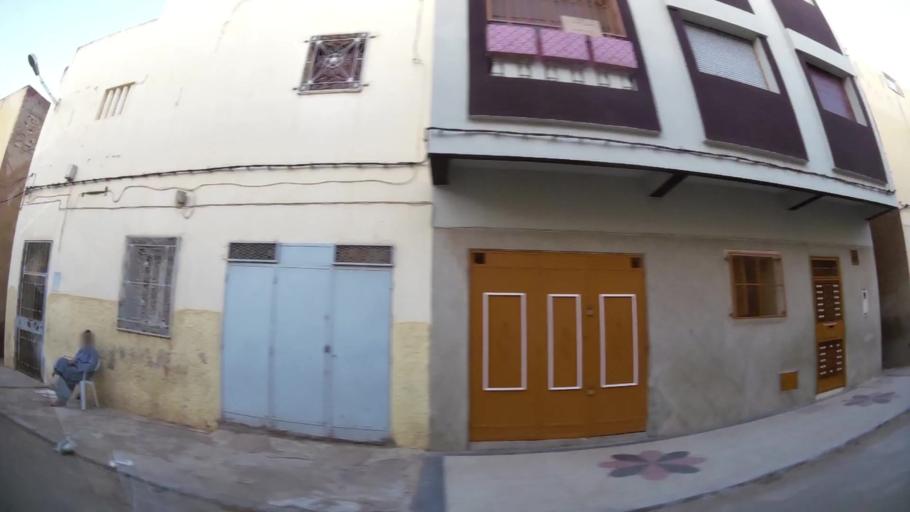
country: MA
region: Oriental
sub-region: Oujda-Angad
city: Oujda
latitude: 34.7019
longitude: -1.9205
